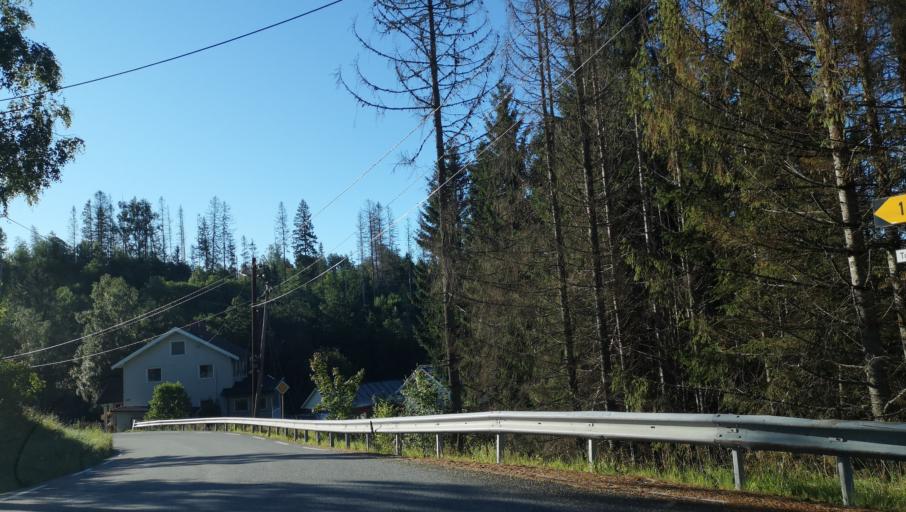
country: NO
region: Ostfold
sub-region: Hobol
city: Tomter
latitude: 59.6556
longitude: 11.0016
